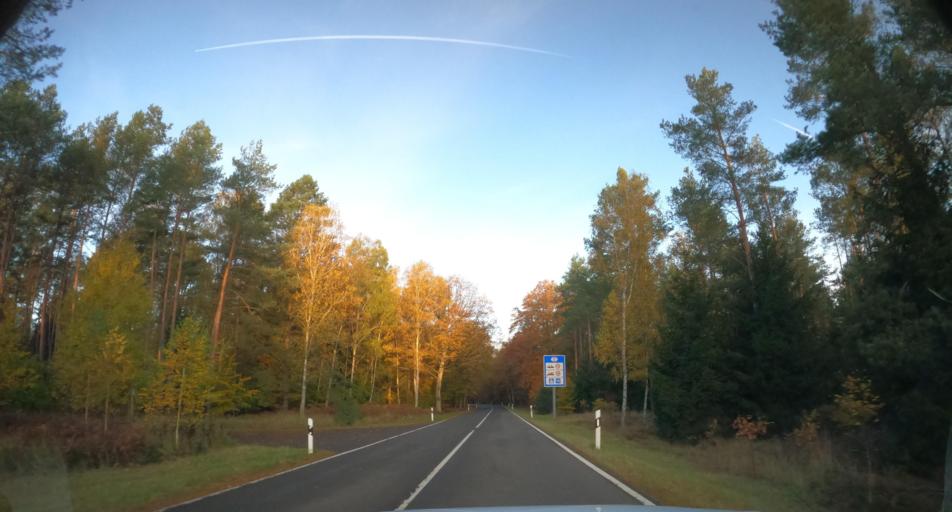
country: PL
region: West Pomeranian Voivodeship
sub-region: Powiat policki
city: Nowe Warpno
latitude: 53.6095
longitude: 14.3155
